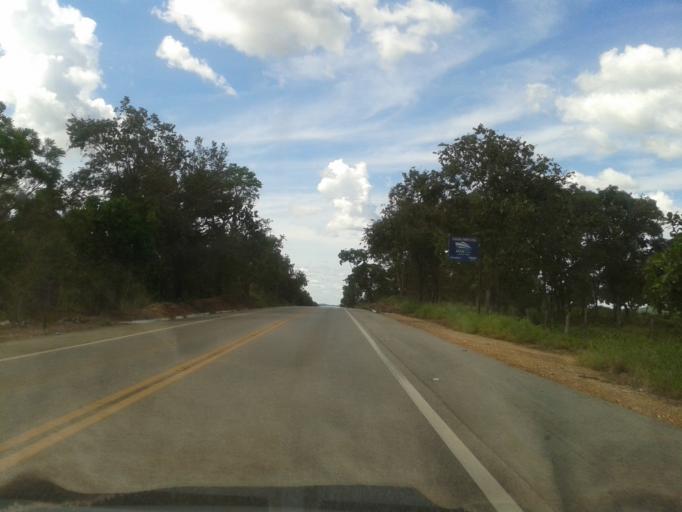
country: BR
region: Goias
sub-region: Itapuranga
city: Itapuranga
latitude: -15.5077
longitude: -50.3026
